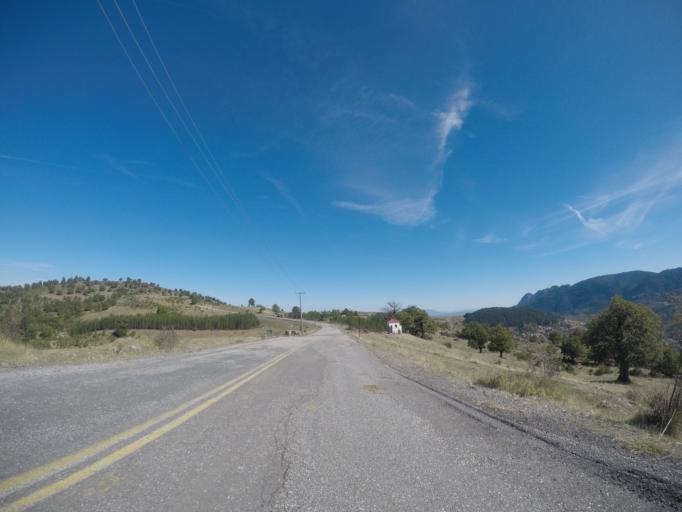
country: GR
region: West Macedonia
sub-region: Nomos Grevenon
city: Grevena
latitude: 40.0556
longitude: 21.1879
